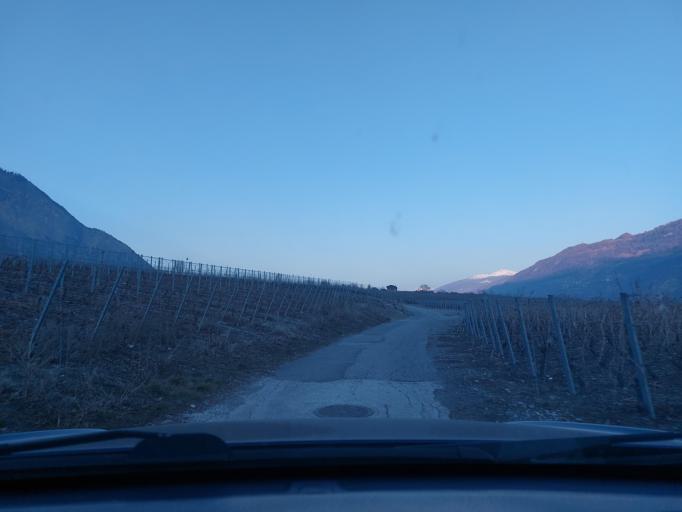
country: CH
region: Valais
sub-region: Martigny District
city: Leytron
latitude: 46.1884
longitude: 7.2158
